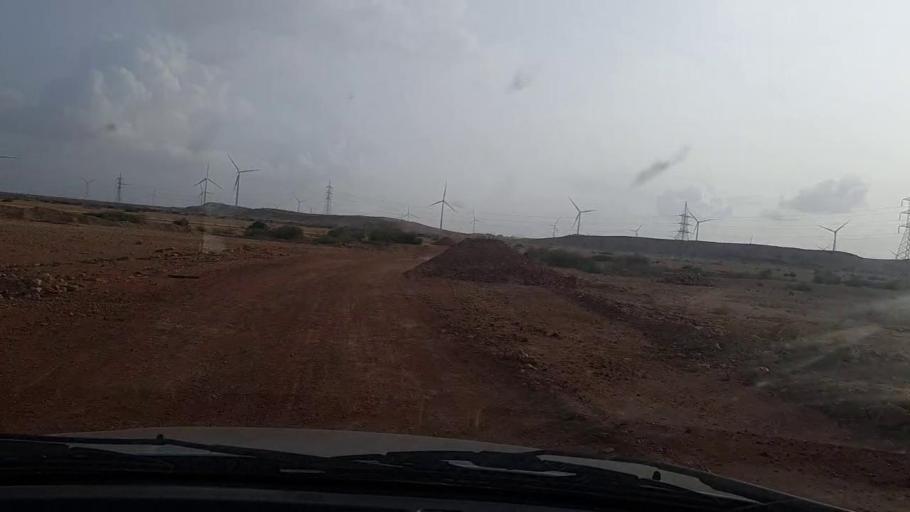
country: PK
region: Sindh
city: Thatta
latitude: 25.0541
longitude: 67.8757
